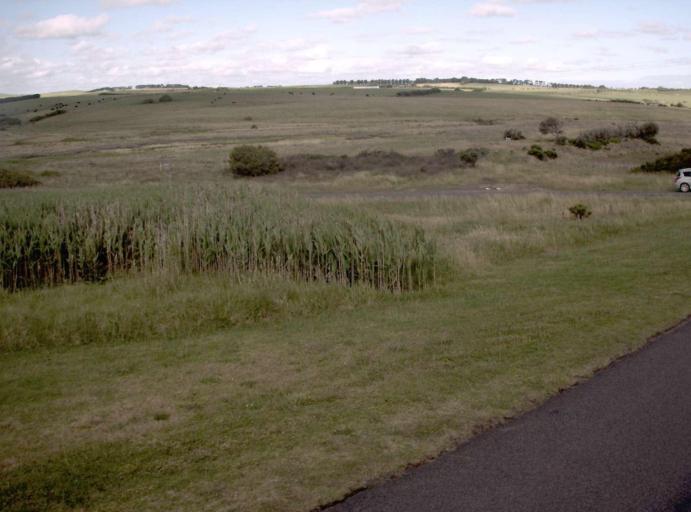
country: AU
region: Victoria
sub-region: Bass Coast
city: North Wonthaggi
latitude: -38.5534
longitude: 145.4811
